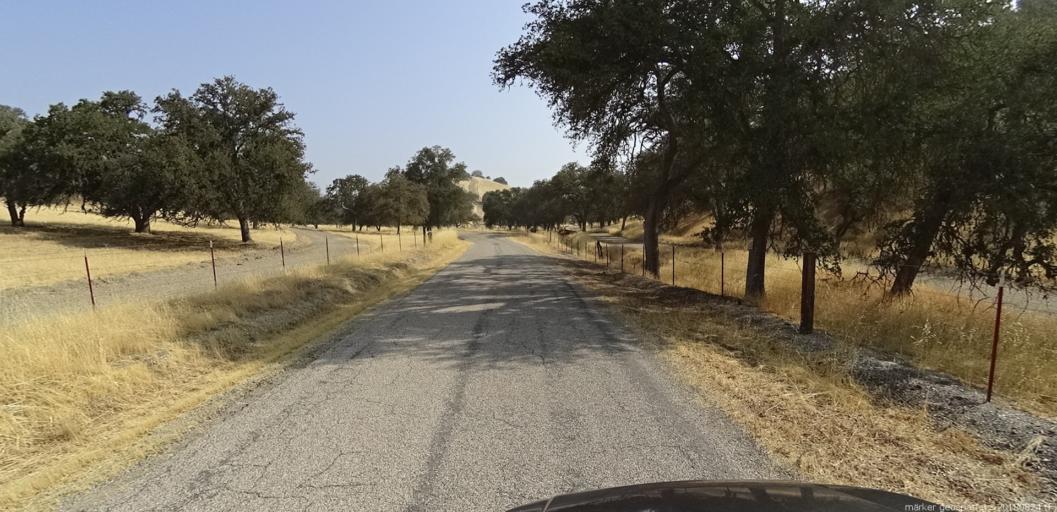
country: US
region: California
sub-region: San Luis Obispo County
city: San Miguel
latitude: 35.8825
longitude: -120.7435
